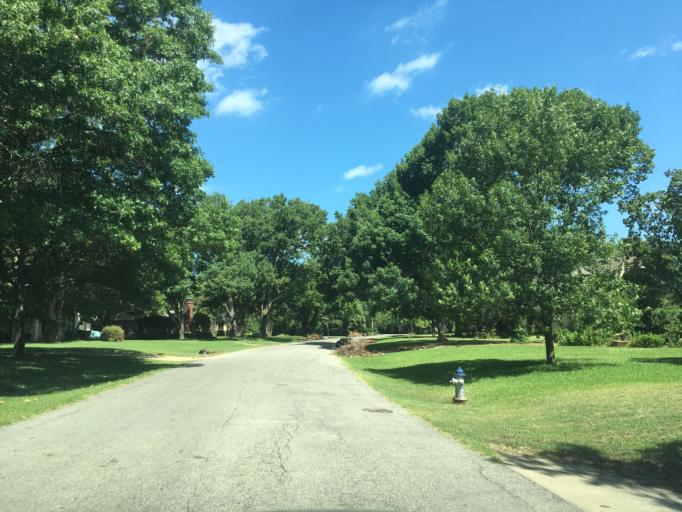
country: US
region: Texas
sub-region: Dallas County
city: Highland Park
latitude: 32.8327
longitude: -96.6946
